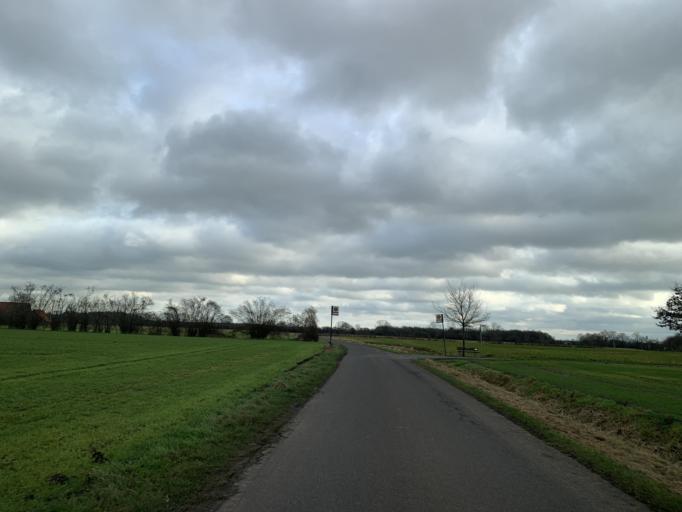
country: DE
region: North Rhine-Westphalia
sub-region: Regierungsbezirk Munster
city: Ascheberg
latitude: 51.8070
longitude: 7.5901
